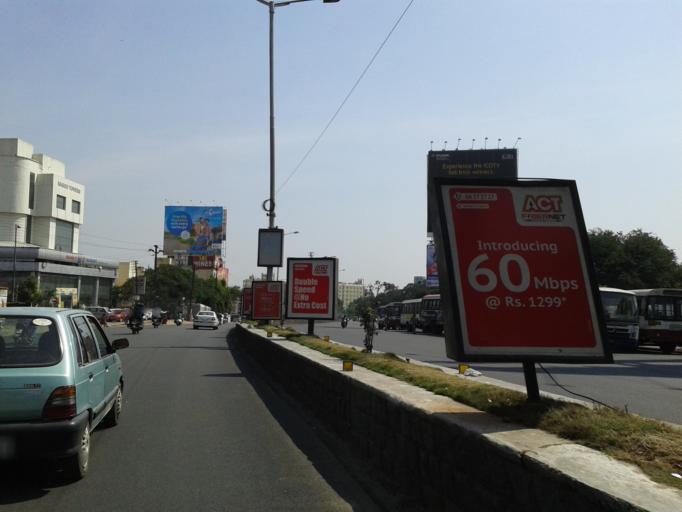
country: IN
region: Telangana
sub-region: Hyderabad
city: Malkajgiri
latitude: 17.4407
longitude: 78.5066
